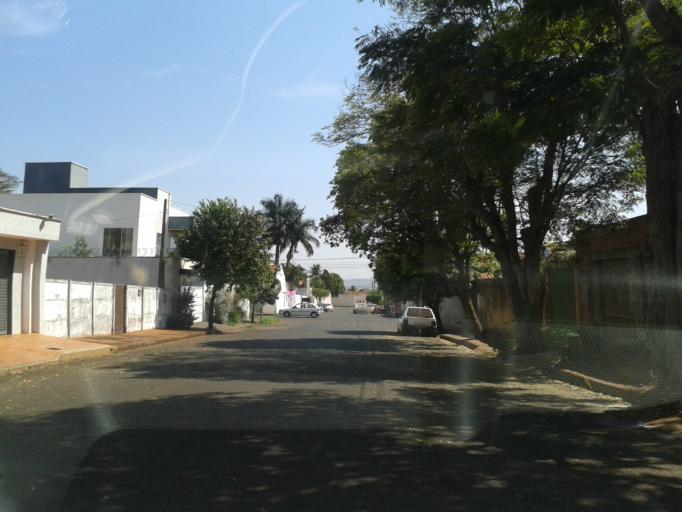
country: BR
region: Minas Gerais
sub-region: Ituiutaba
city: Ituiutaba
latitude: -18.9902
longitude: -49.4552
